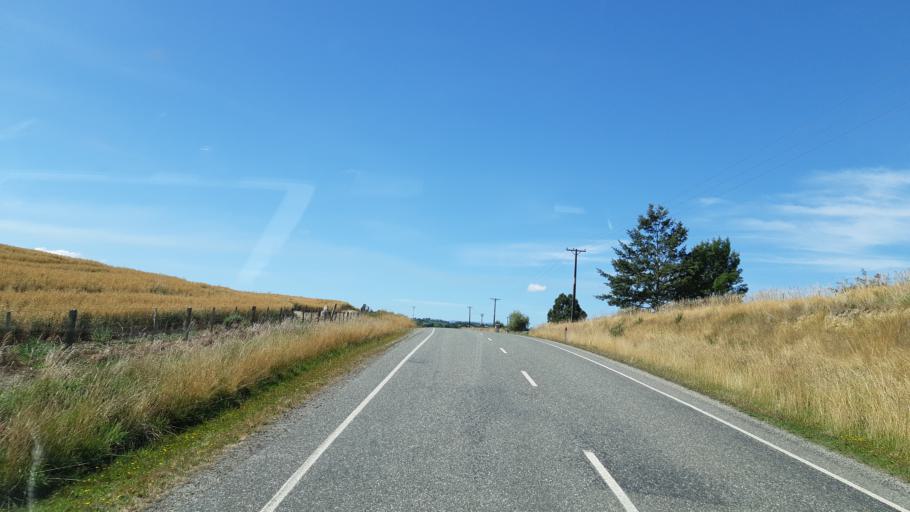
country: NZ
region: Southland
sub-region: Gore District
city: Gore
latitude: -46.0044
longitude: 168.8987
